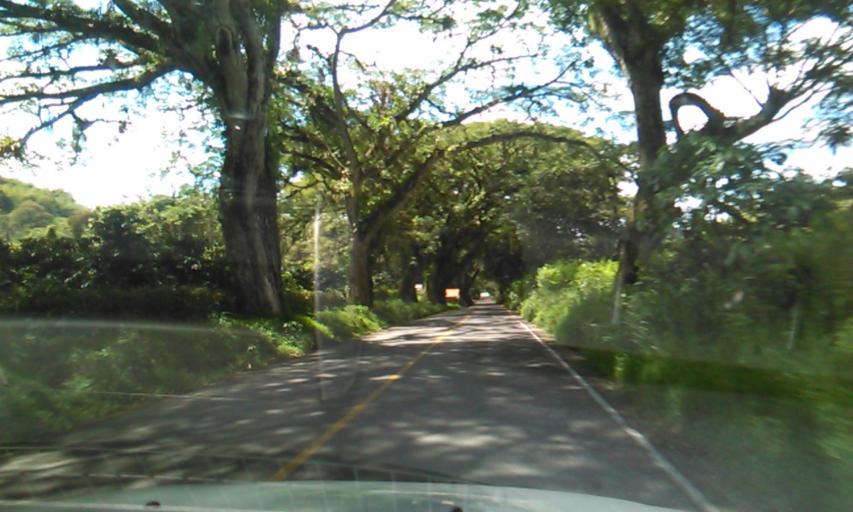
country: CO
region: Quindio
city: Cordoba
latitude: 4.4051
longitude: -75.7070
